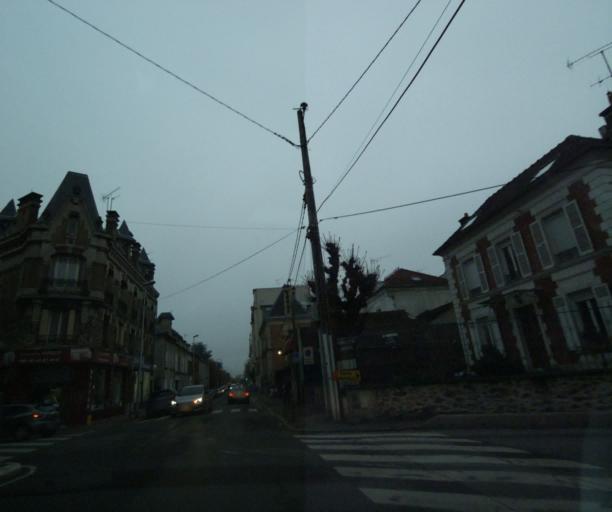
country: FR
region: Ile-de-France
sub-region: Departement de Seine-Saint-Denis
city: Le Raincy
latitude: 48.8900
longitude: 2.5134
